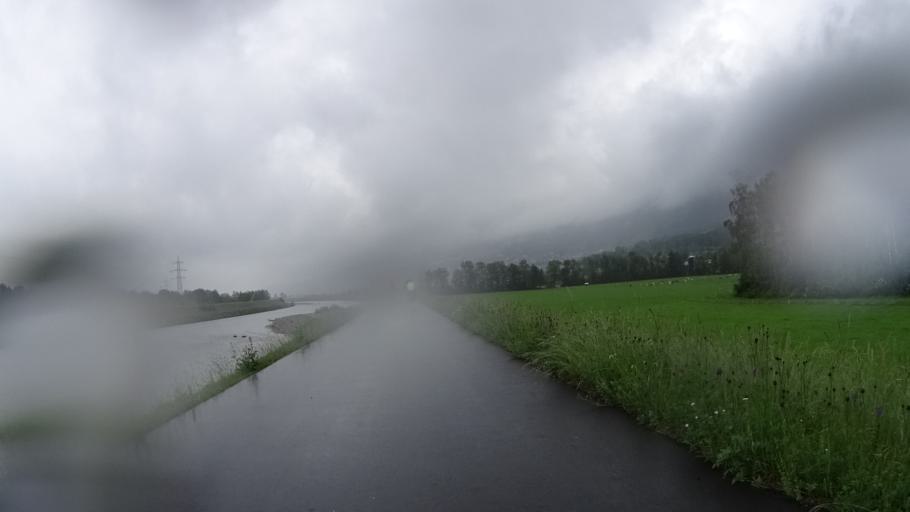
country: LI
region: Triesen
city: Triesen
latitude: 47.0902
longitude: 9.5177
